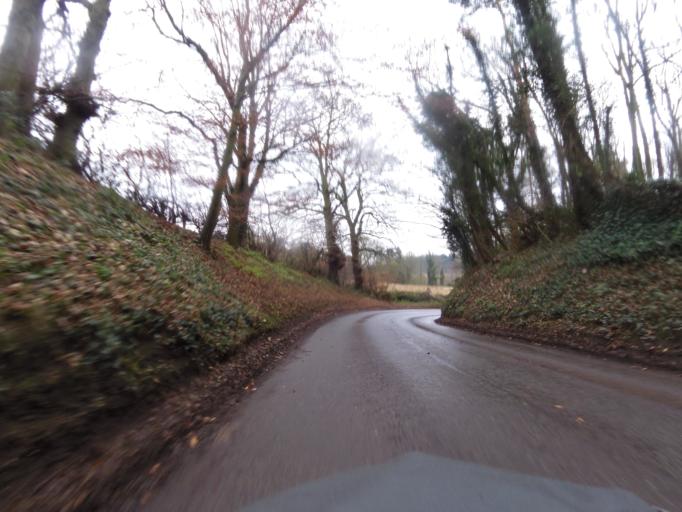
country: GB
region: England
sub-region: Norfolk
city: Briston
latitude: 52.8760
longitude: 1.0758
